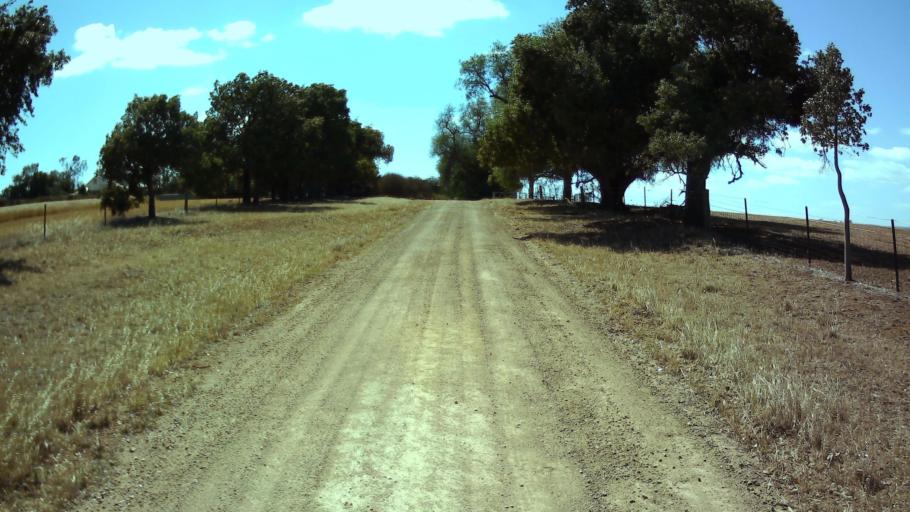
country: AU
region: New South Wales
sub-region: Weddin
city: Grenfell
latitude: -33.9647
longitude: 148.4122
